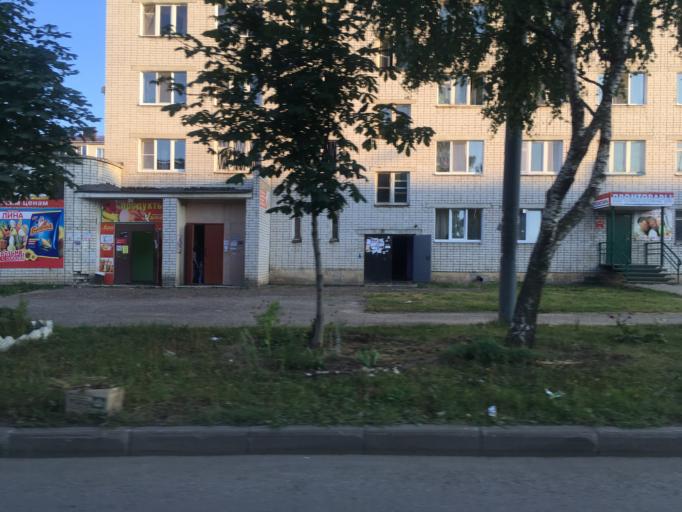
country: RU
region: Mariy-El
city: Yoshkar-Ola
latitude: 56.6499
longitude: 47.8648
